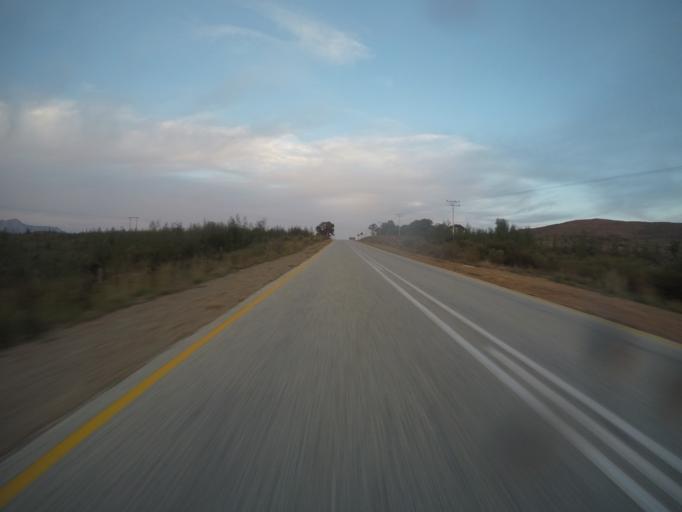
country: ZA
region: Western Cape
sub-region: Eden District Municipality
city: Plettenberg Bay
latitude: -33.7400
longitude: 23.4327
